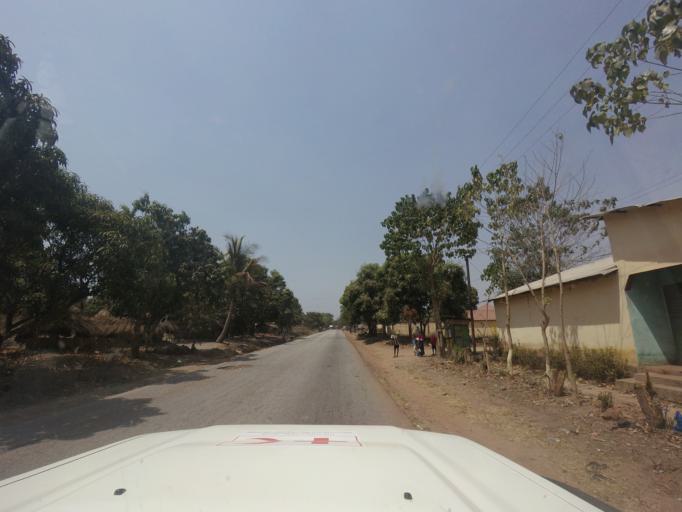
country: GN
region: Kindia
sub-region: Kindia
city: Kindia
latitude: 9.9242
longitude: -12.9926
